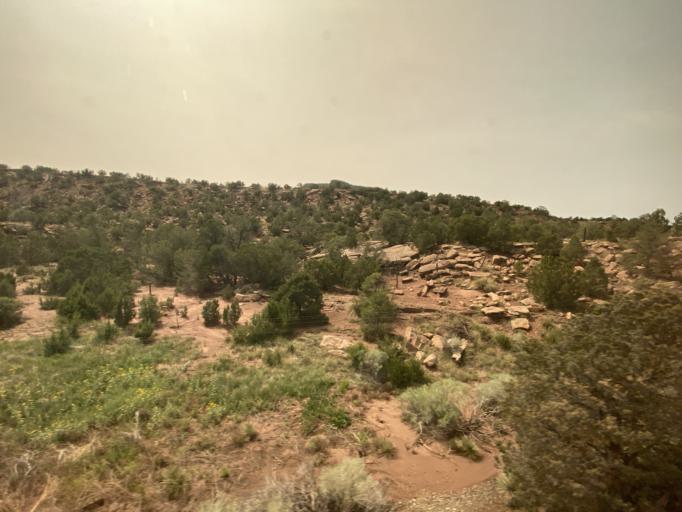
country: US
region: New Mexico
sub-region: San Miguel County
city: Pecos
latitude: 35.3999
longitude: -105.4945
